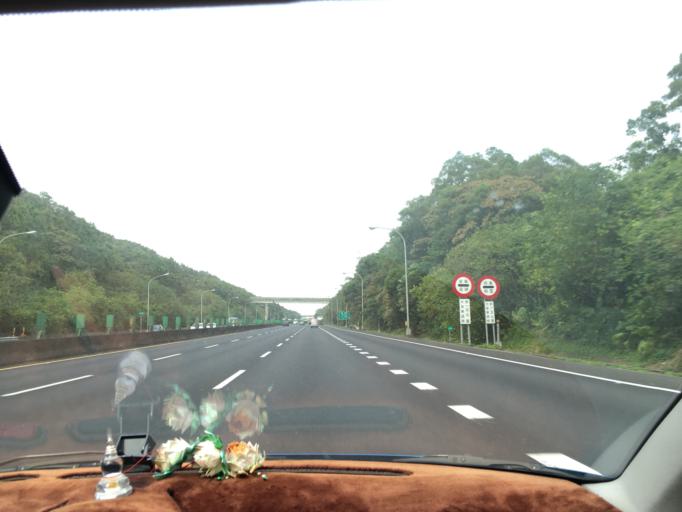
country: TW
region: Taiwan
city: Daxi
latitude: 24.8150
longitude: 121.2005
